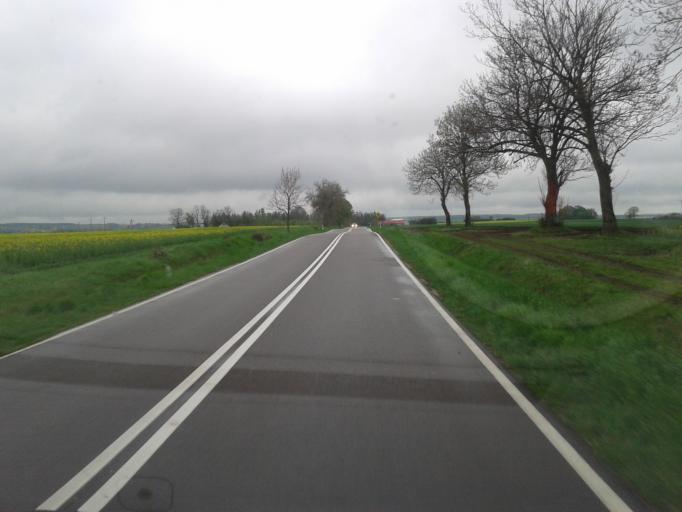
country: PL
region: Lublin Voivodeship
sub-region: Powiat tomaszowski
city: Telatyn
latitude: 50.5461
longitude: 23.9275
